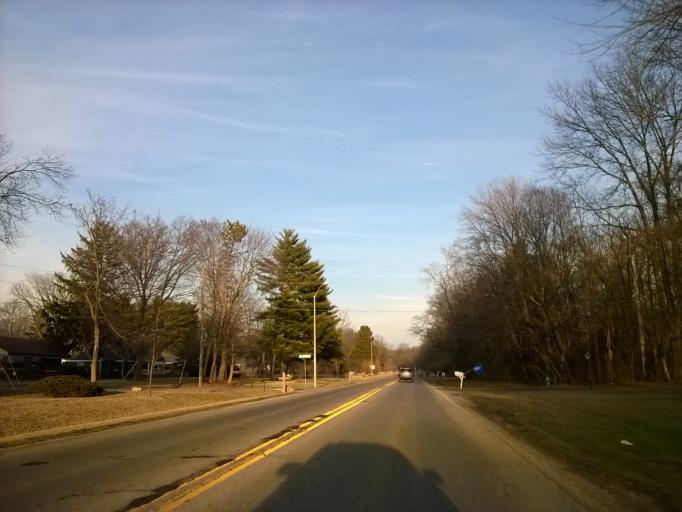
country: US
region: Indiana
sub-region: Marion County
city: Meridian Hills
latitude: 39.8576
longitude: -86.1840
